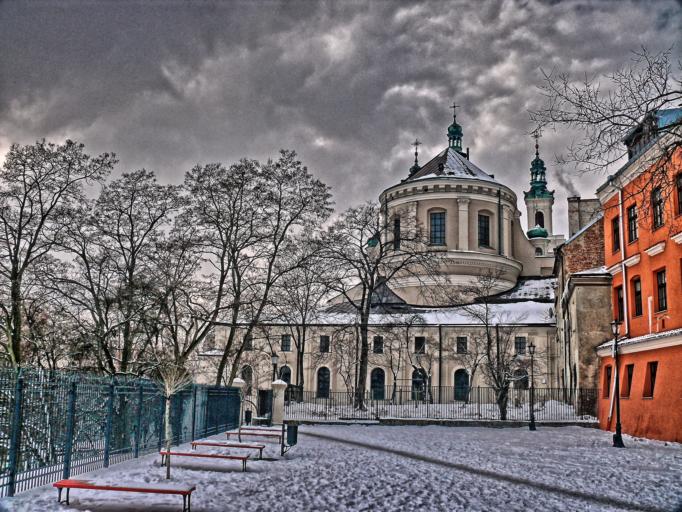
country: PL
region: Lublin Voivodeship
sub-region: Powiat lubelski
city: Lublin
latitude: 51.2470
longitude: 22.5704
